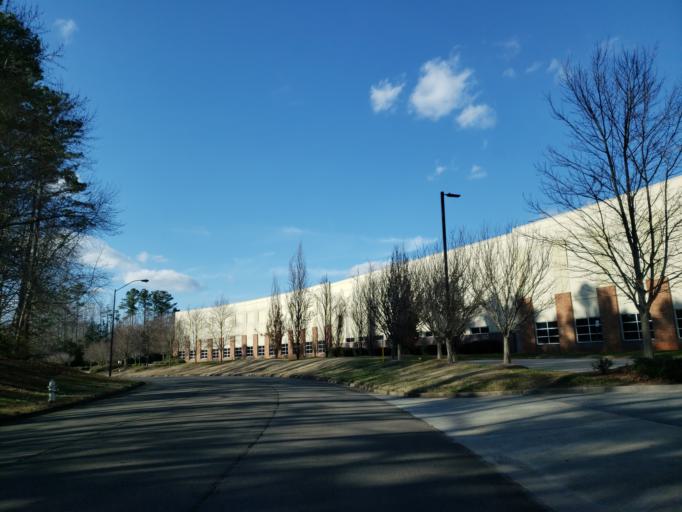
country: US
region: Georgia
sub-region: Cobb County
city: Marietta
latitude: 33.9894
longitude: -84.5204
